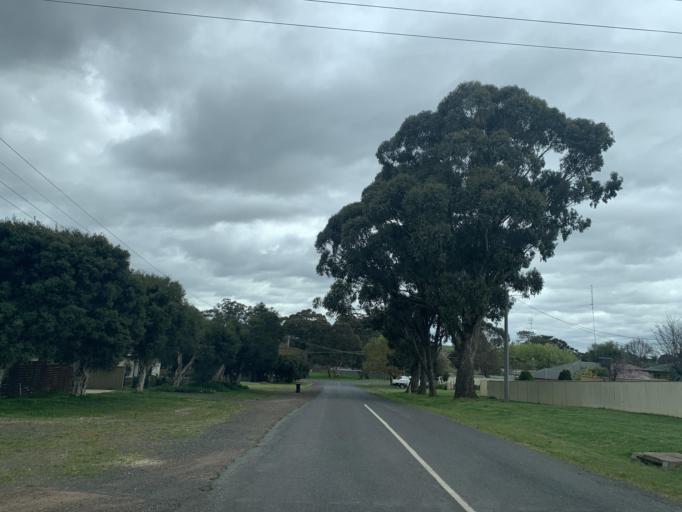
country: AU
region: Victoria
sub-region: Whittlesea
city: Whittlesea
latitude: -37.2099
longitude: 145.0429
